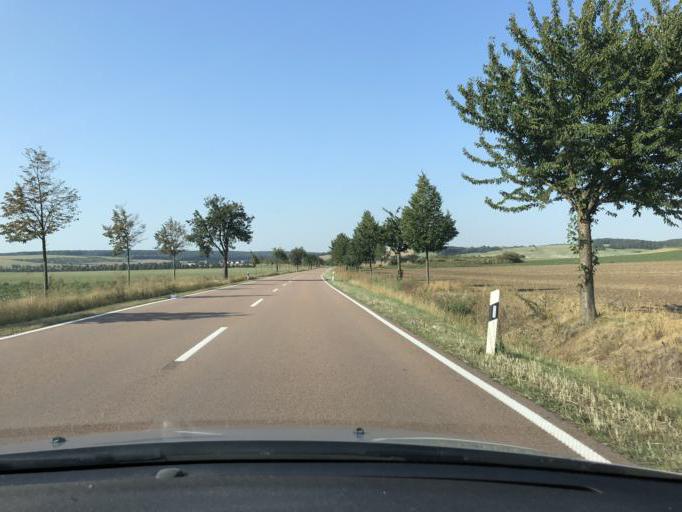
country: DE
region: Saxony-Anhalt
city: Krumpa
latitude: 51.2525
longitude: 11.8468
